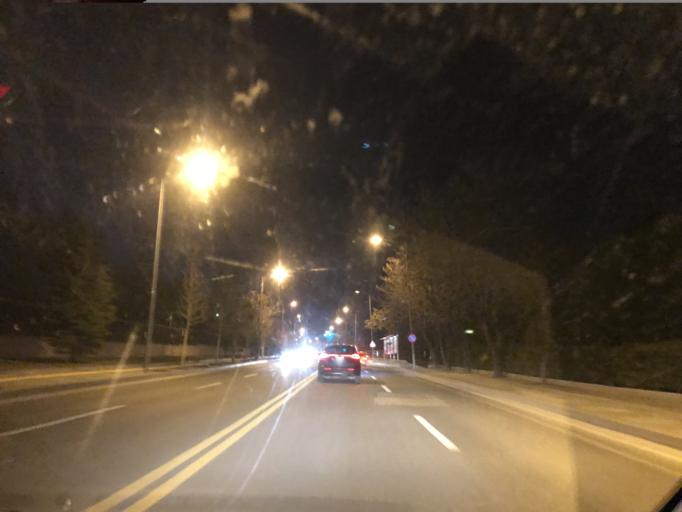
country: TR
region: Ankara
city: Cankaya
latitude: 39.8795
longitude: 32.8656
